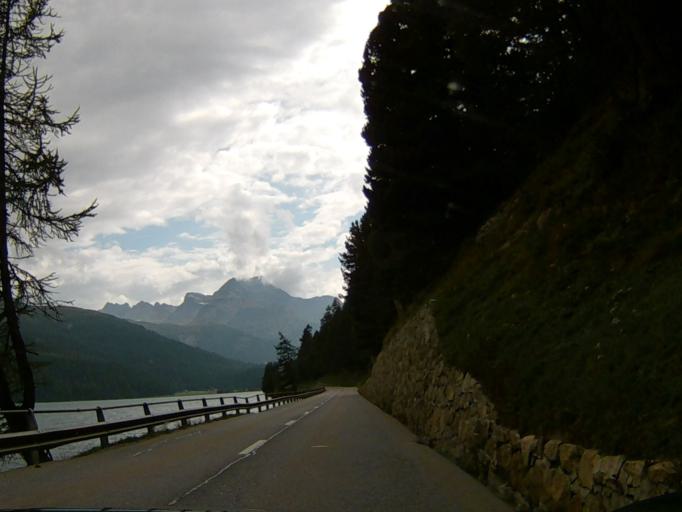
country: CH
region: Grisons
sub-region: Maloja District
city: Silvaplana
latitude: 46.4525
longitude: 9.7873
